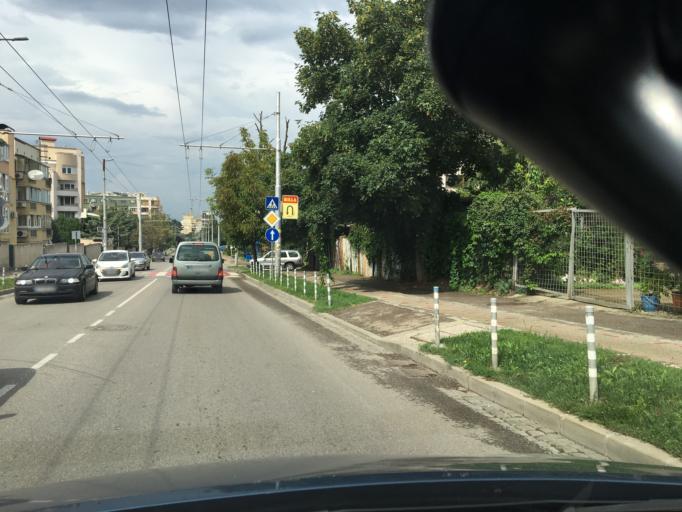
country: BG
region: Sofia-Capital
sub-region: Stolichna Obshtina
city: Sofia
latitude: 42.6610
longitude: 23.2734
